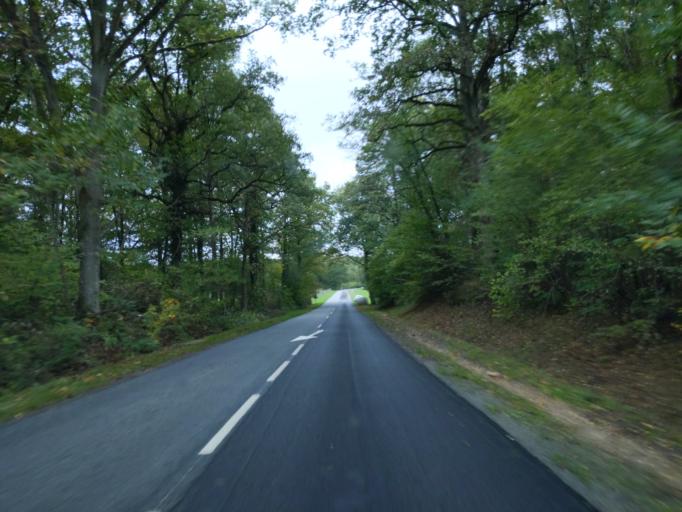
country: FR
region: Ile-de-France
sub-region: Departement des Yvelines
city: Bullion
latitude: 48.5983
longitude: 1.9934
